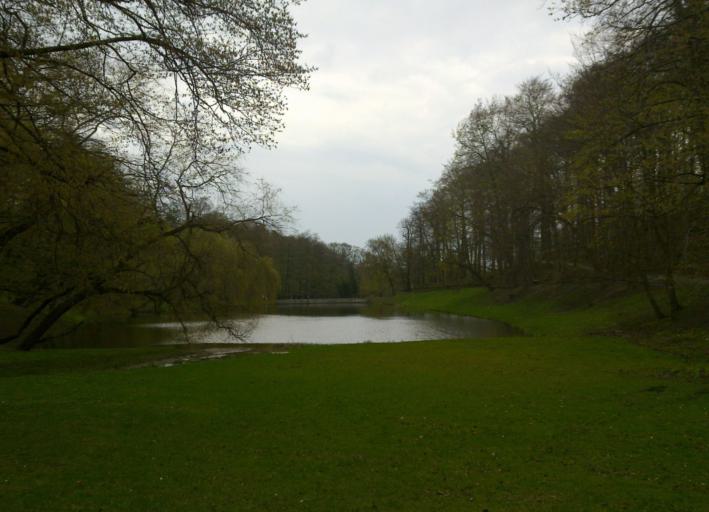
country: PL
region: Pomeranian Voivodeship
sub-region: Gdansk
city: Gdansk
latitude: 54.3210
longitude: 18.6237
